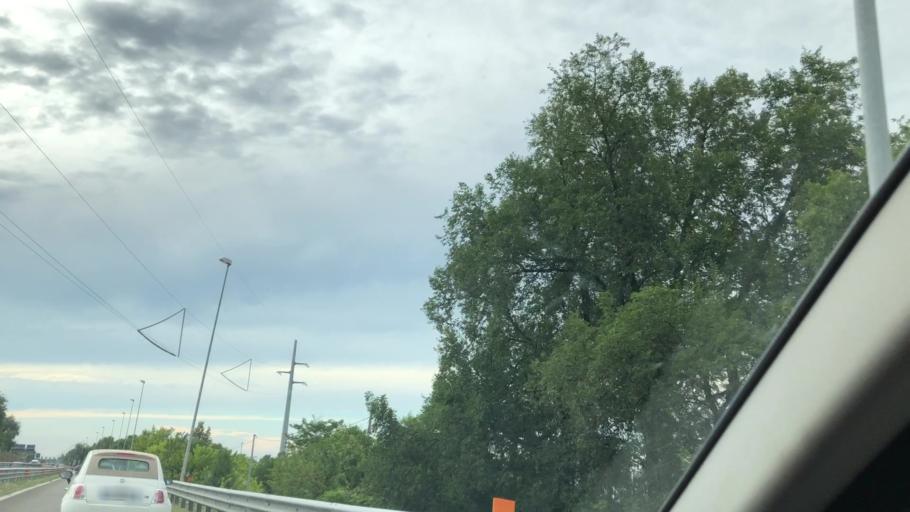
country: IT
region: Emilia-Romagna
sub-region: Provincia di Bologna
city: Calderara di Reno
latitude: 44.5205
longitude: 11.2805
